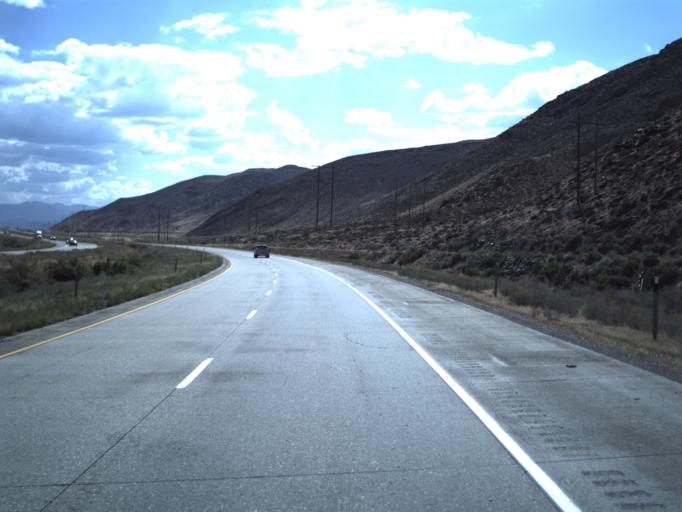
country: US
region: Utah
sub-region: Sevier County
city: Richfield
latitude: 38.7282
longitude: -112.1277
